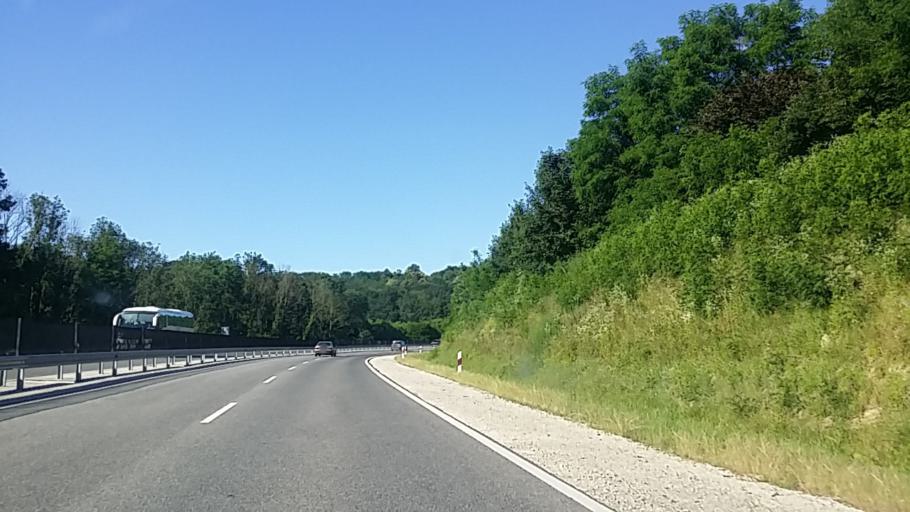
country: HU
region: Zala
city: Zalaegerszeg
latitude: 46.8360
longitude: 16.8913
